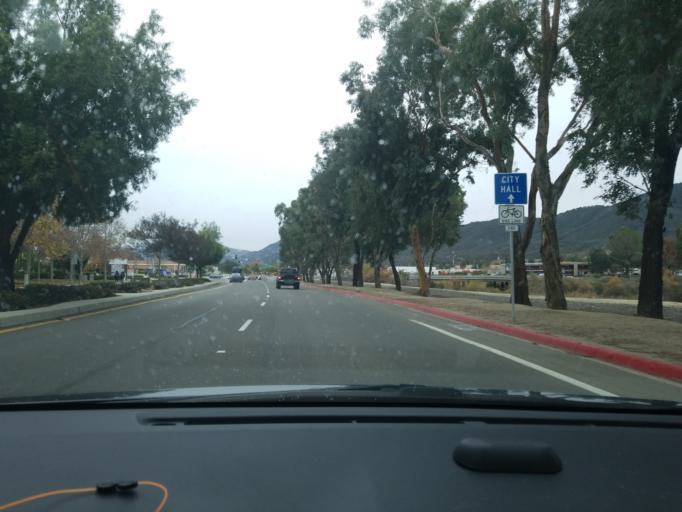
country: US
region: California
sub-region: Riverside County
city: Temecula
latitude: 33.5009
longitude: -117.1546
